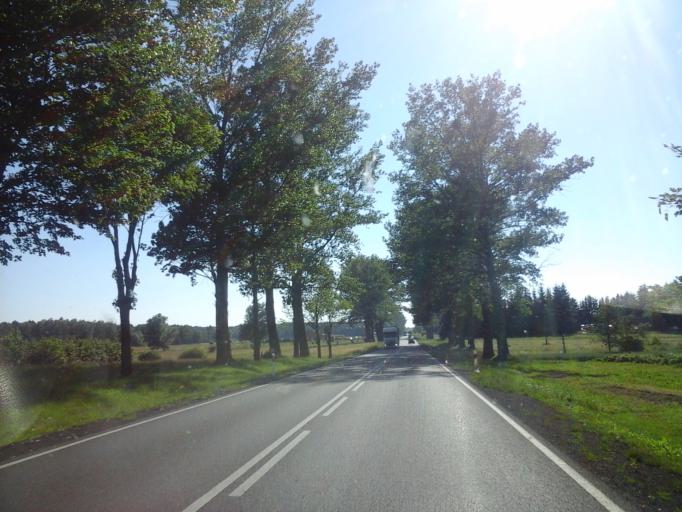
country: PL
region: West Pomeranian Voivodeship
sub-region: Powiat gryficki
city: Ploty
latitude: 53.8532
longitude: 15.3340
